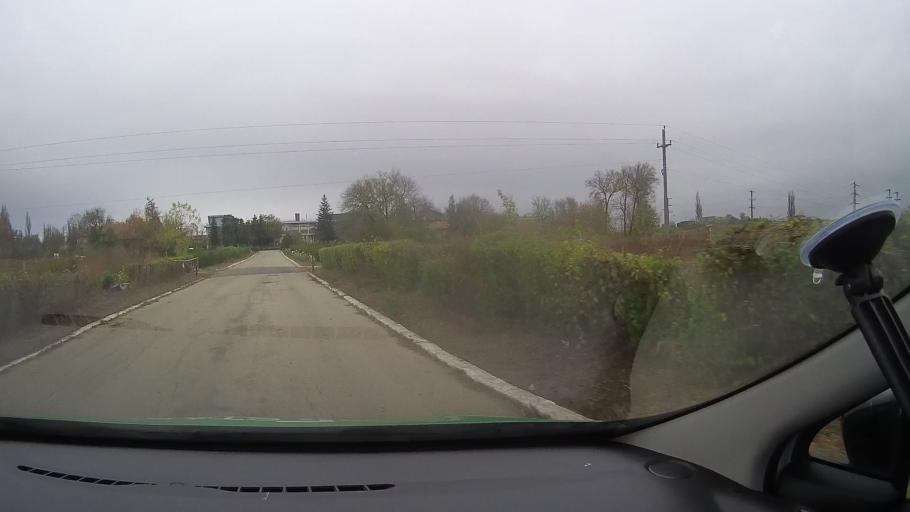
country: RO
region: Constanta
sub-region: Oras Murfatlar
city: Murfatlar
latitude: 44.1757
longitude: 28.4228
